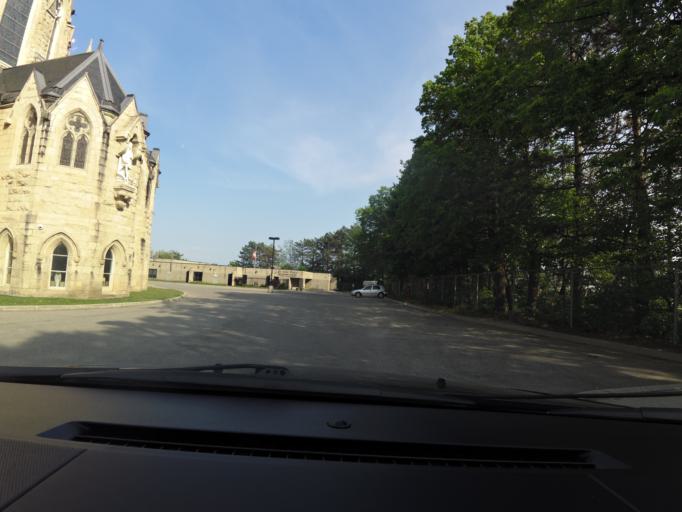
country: CA
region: Ontario
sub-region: Wellington County
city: Guelph
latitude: 43.5429
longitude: -80.2523
